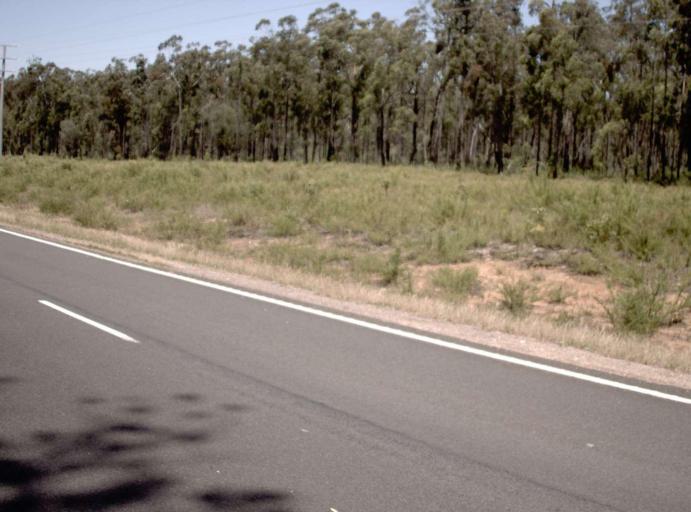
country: AU
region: Victoria
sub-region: East Gippsland
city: Lakes Entrance
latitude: -37.7343
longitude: 148.1455
